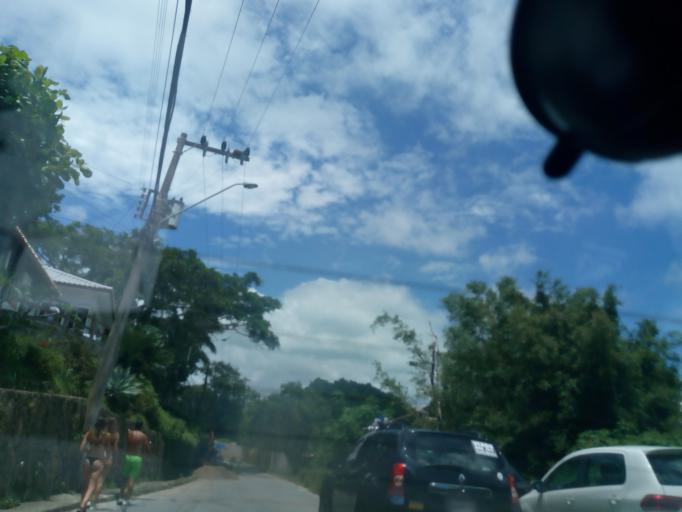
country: BR
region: Santa Catarina
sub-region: Florianopolis
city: Itacorubi
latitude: -27.3917
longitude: -48.4210
